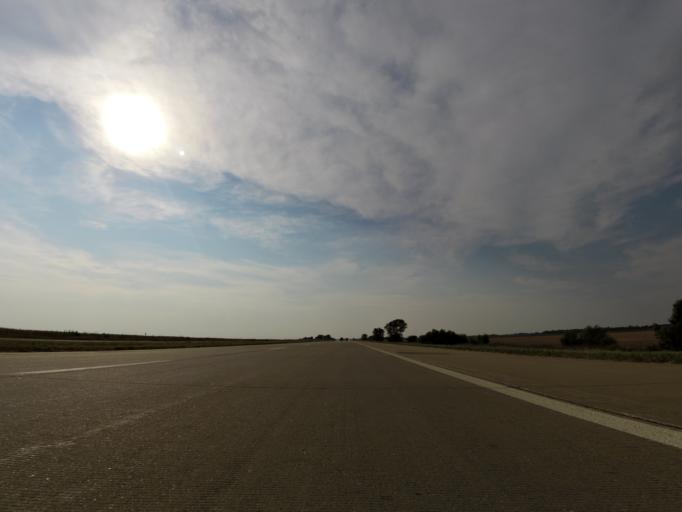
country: US
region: Kansas
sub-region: Sedgwick County
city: Colwich
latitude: 37.8426
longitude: -97.5786
